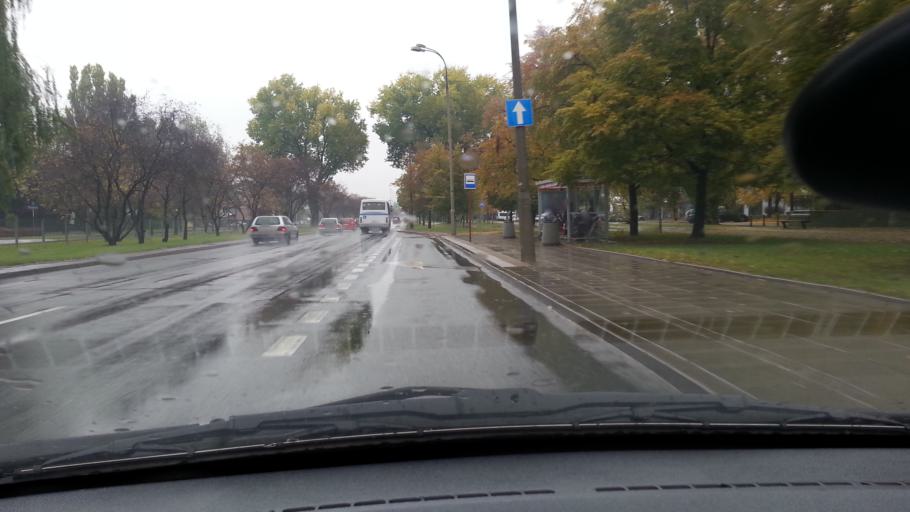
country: PL
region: Masovian Voivodeship
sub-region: Warszawa
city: Targowek
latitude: 52.2863
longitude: 21.0221
